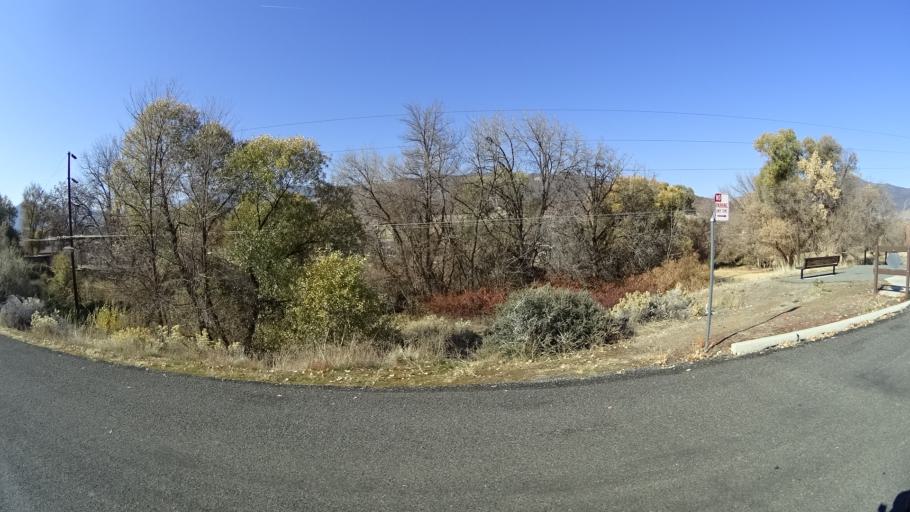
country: US
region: California
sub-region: Siskiyou County
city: Yreka
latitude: 41.7419
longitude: -122.6288
